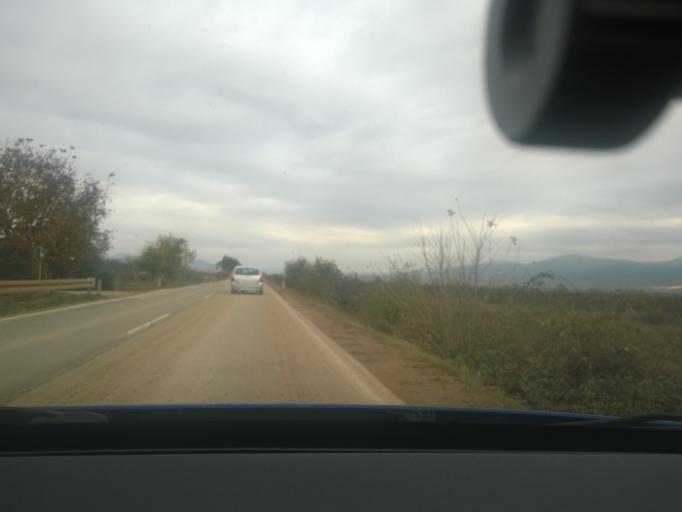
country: RS
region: Central Serbia
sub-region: Pirotski Okrug
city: Pirot
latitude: 43.0733
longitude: 22.6703
